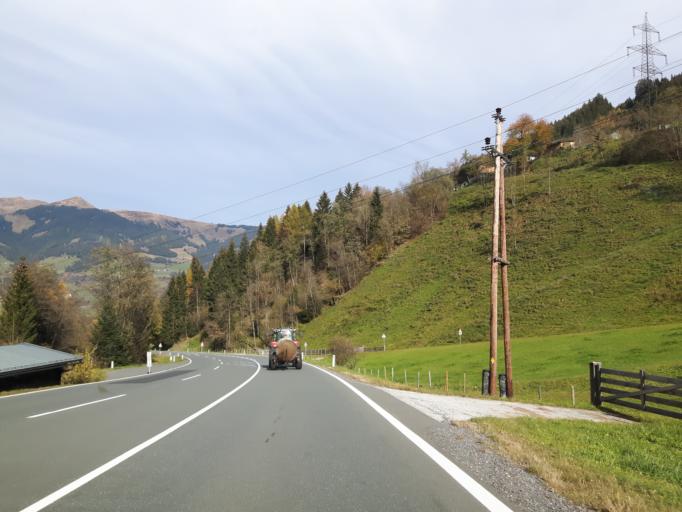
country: AT
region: Salzburg
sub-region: Politischer Bezirk Zell am See
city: Mittersill
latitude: 47.2601
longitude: 12.4842
